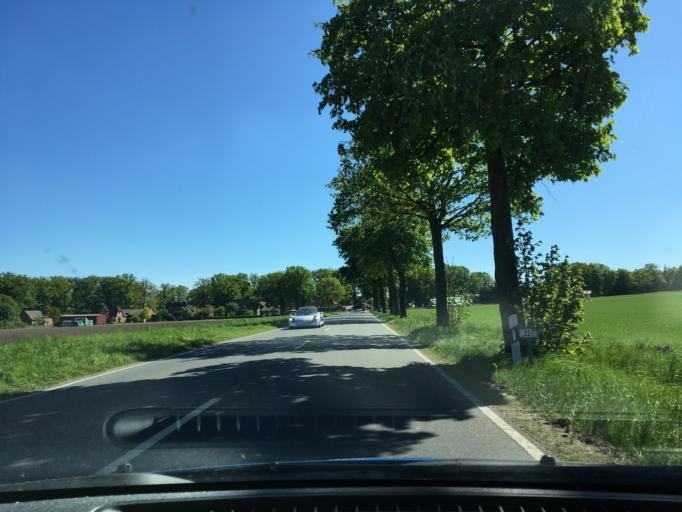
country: DE
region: Lower Saxony
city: Hermannsburg
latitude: 52.8516
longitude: 10.0816
